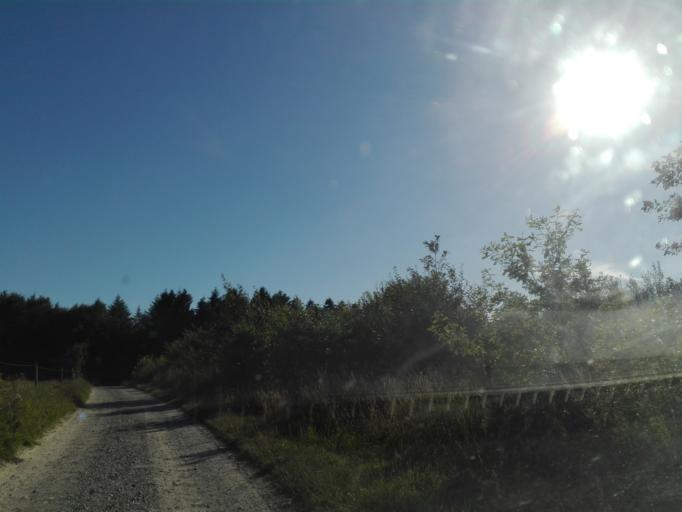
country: DK
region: North Denmark
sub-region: Mariagerfjord Kommune
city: Mariager
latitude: 56.6633
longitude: 9.9479
